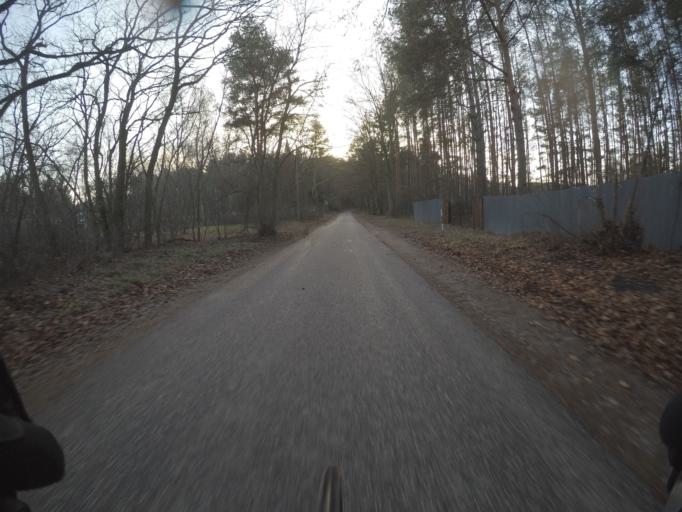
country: DE
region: Brandenburg
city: Hohen Neuendorf
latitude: 52.6857
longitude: 13.2607
